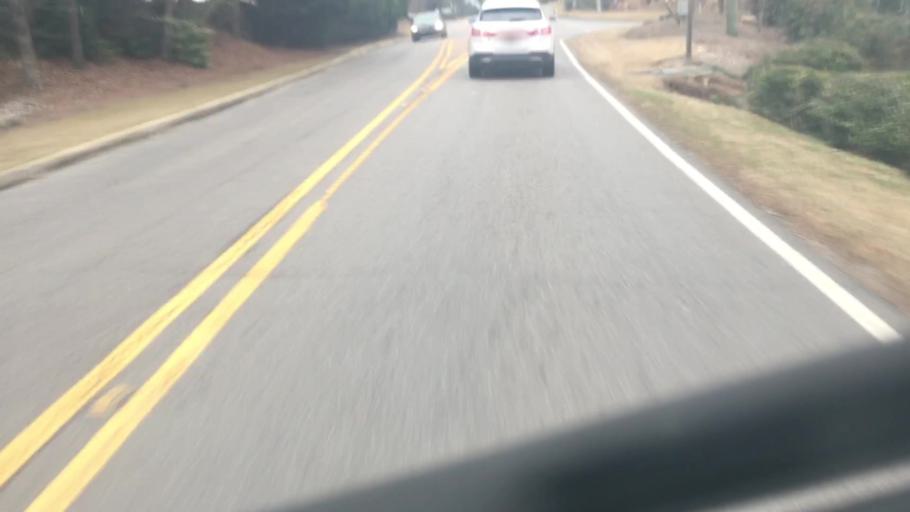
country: US
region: Alabama
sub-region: Jefferson County
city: Hoover
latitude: 33.3709
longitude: -86.8089
